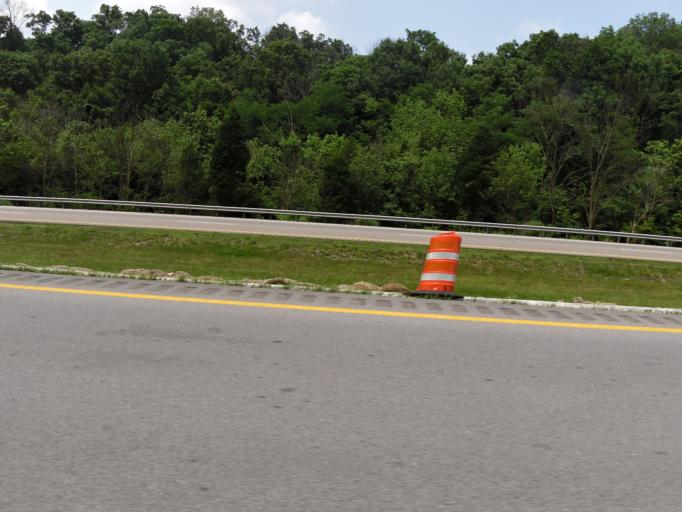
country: US
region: Kentucky
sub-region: Carroll County
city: Carrollton
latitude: 38.6540
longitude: -85.1085
